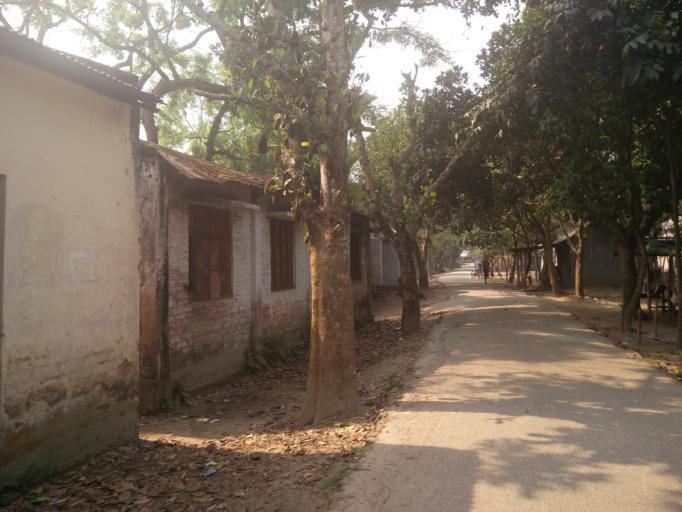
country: BD
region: Dhaka
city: Sherpur
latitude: 24.9124
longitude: 90.1560
